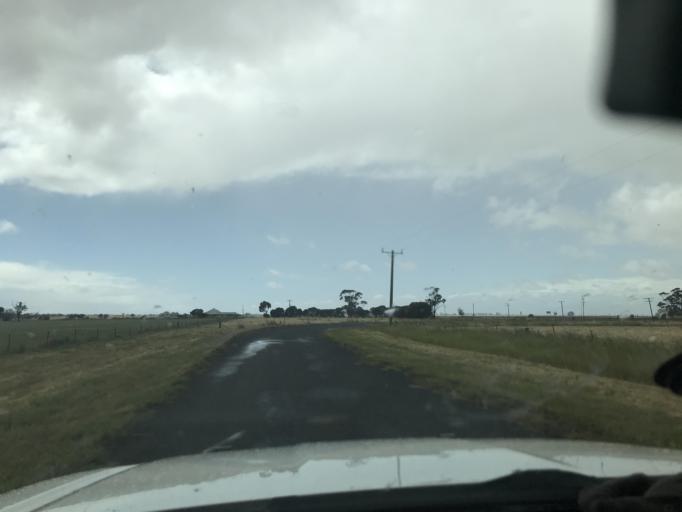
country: AU
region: South Australia
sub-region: Tatiara
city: Bordertown
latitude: -36.3743
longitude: 140.9885
